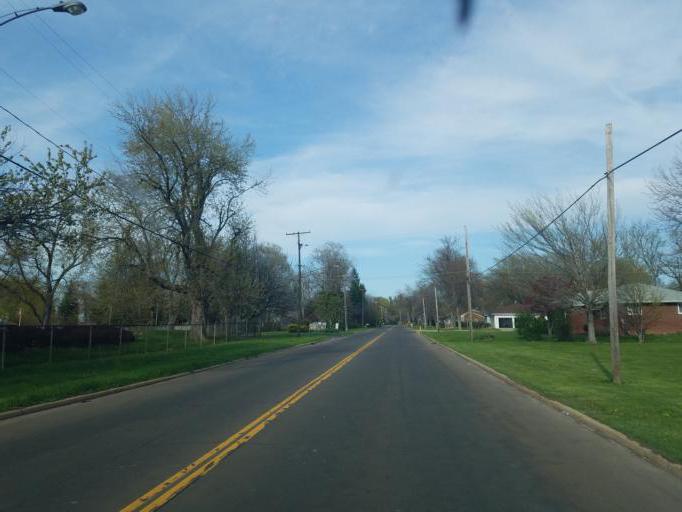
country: US
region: Ohio
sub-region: Ashtabula County
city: Ashtabula
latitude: 41.8913
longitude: -80.8298
